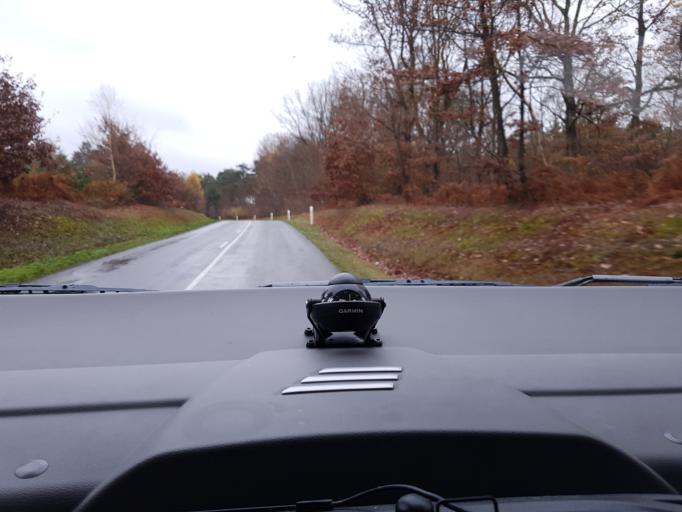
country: FR
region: Haute-Normandie
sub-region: Departement de l'Eure
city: Pont-Saint-Pierre
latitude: 49.3229
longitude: 1.2937
